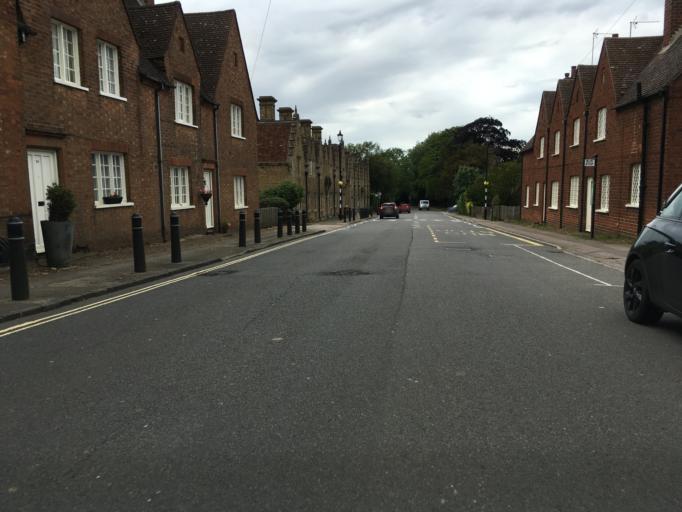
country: GB
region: England
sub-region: Central Bedfordshire
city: Woburn
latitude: 51.9905
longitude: -0.6201
